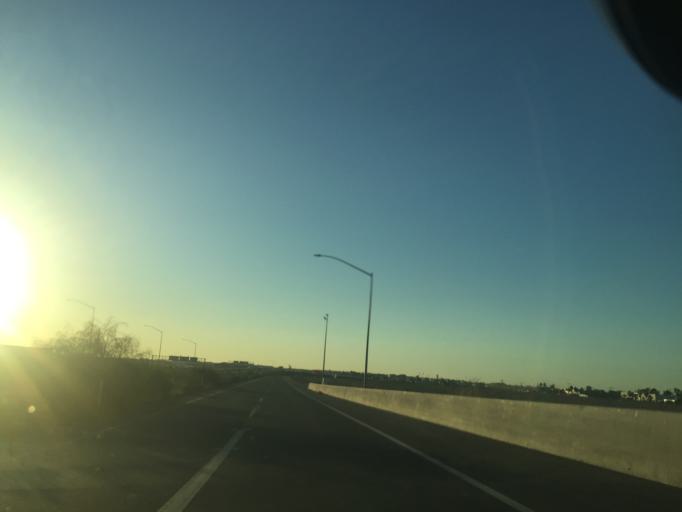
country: MX
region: Baja California
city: Tijuana
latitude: 32.5648
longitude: -116.9517
